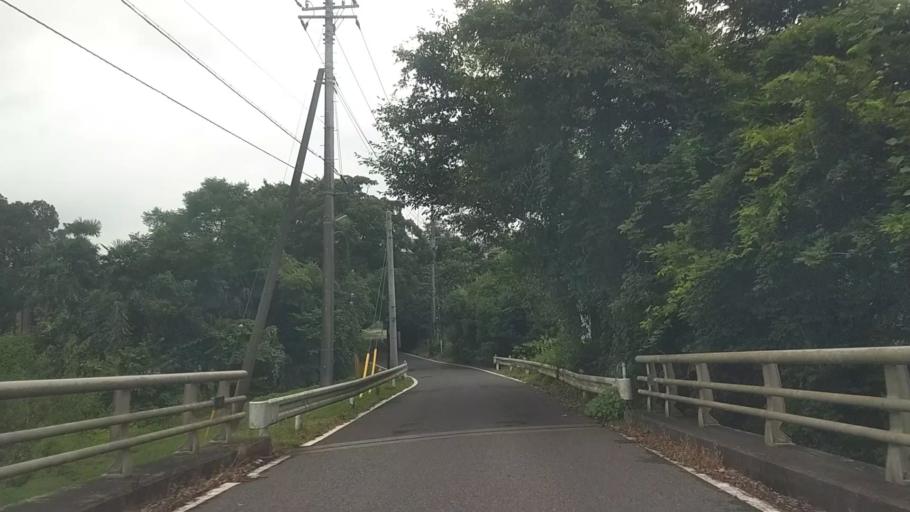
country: JP
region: Chiba
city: Kawaguchi
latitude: 35.2576
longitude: 140.0496
